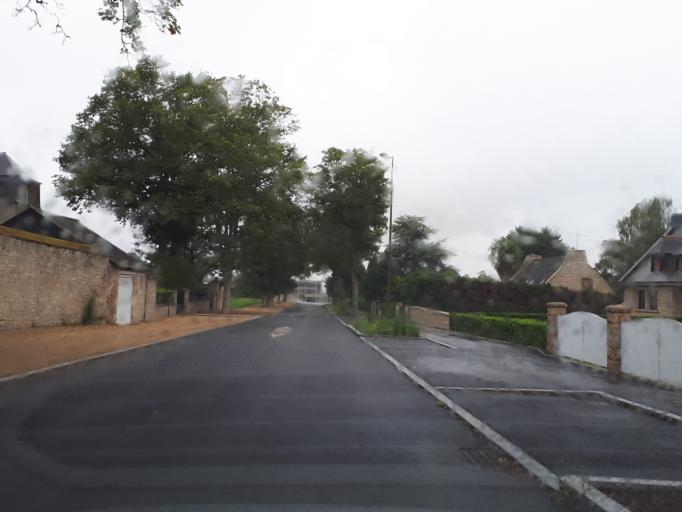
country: FR
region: Brittany
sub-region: Departement des Cotes-d'Armor
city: Broons
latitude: 48.3212
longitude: -2.2639
